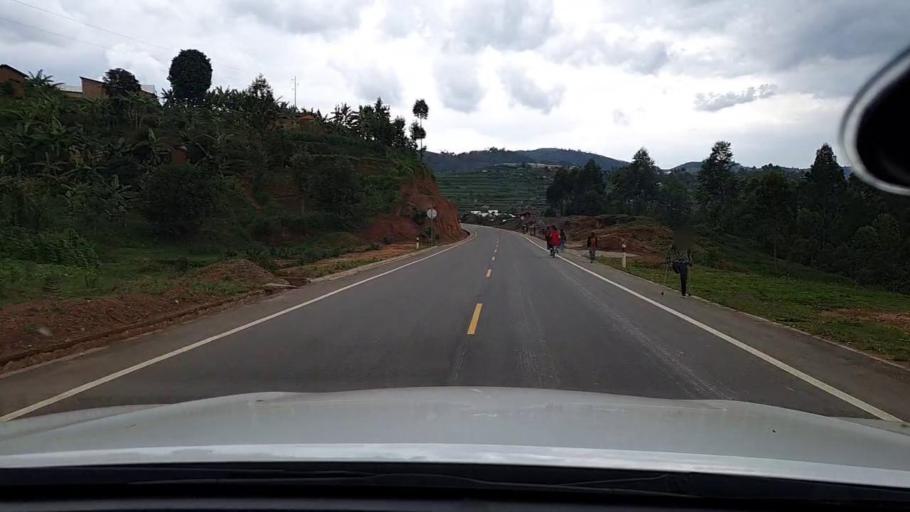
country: RW
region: Northern Province
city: Byumba
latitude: -1.6386
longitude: 29.9270
